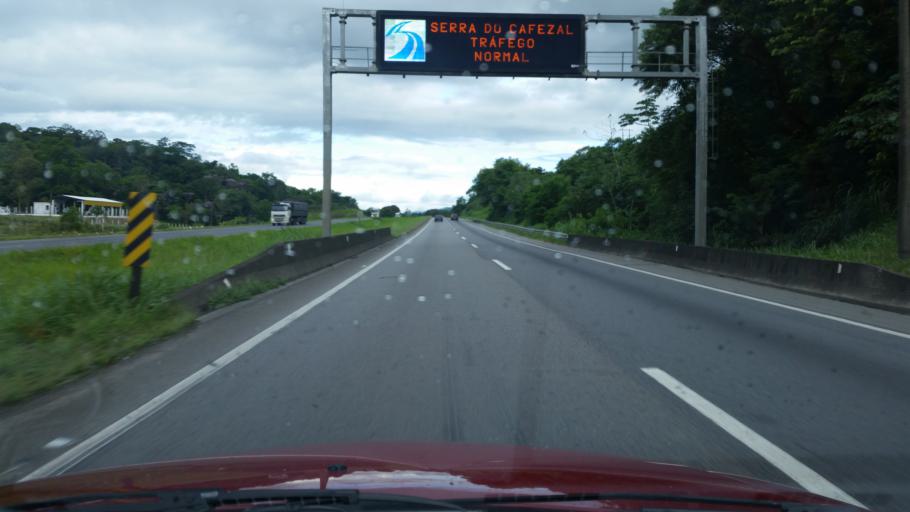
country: BR
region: Sao Paulo
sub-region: Miracatu
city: Miracatu
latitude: -24.2651
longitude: -47.3869
